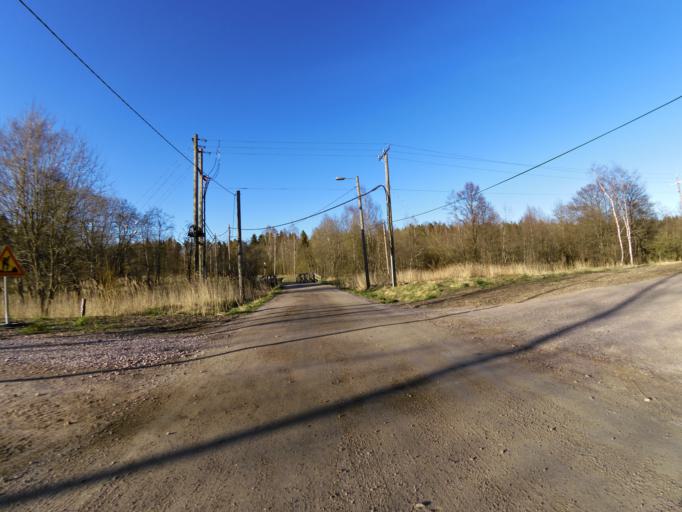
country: FI
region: Uusimaa
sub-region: Helsinki
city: Espoo
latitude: 60.1779
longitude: 24.6893
